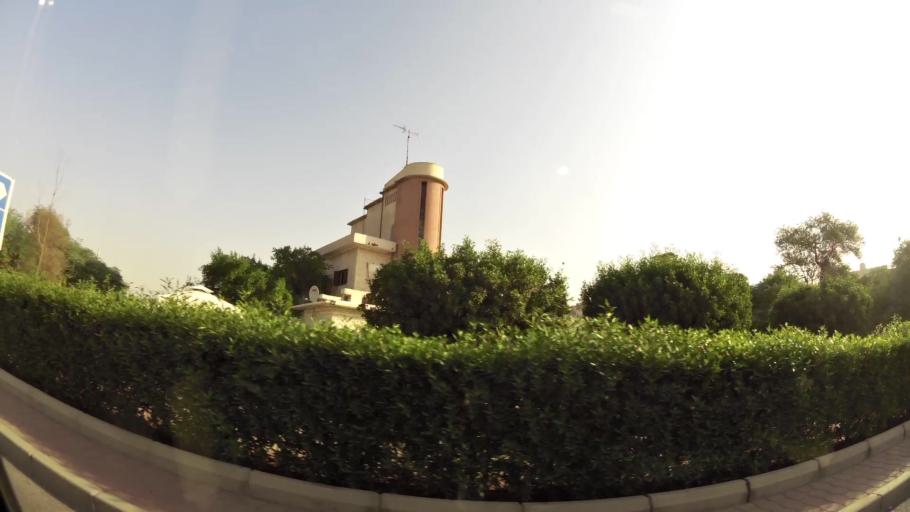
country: KW
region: Al Asimah
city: Ad Dasmah
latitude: 29.3588
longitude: 48.0009
